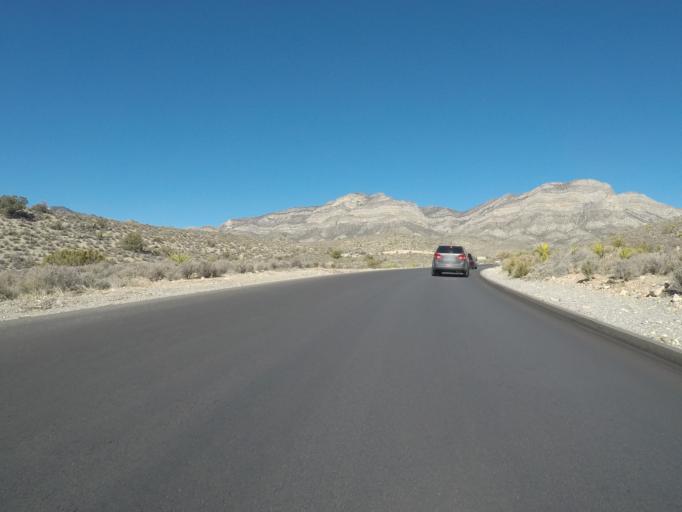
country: US
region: Nevada
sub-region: Clark County
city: Summerlin South
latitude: 36.1699
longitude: -115.4625
